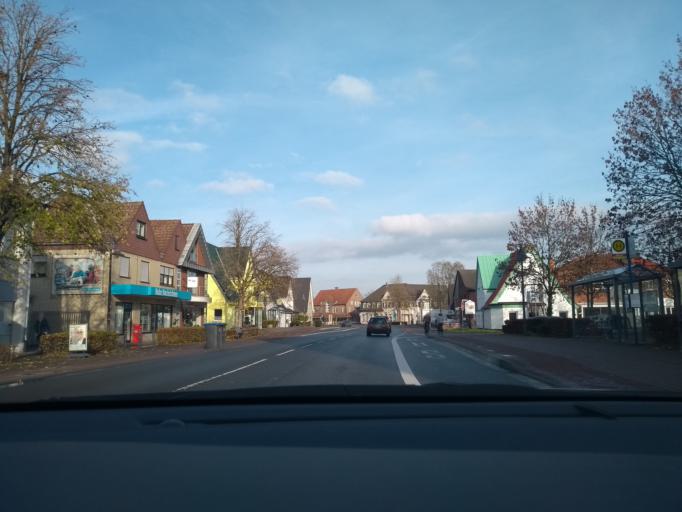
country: DE
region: North Rhine-Westphalia
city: Selm
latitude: 51.6910
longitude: 7.4658
